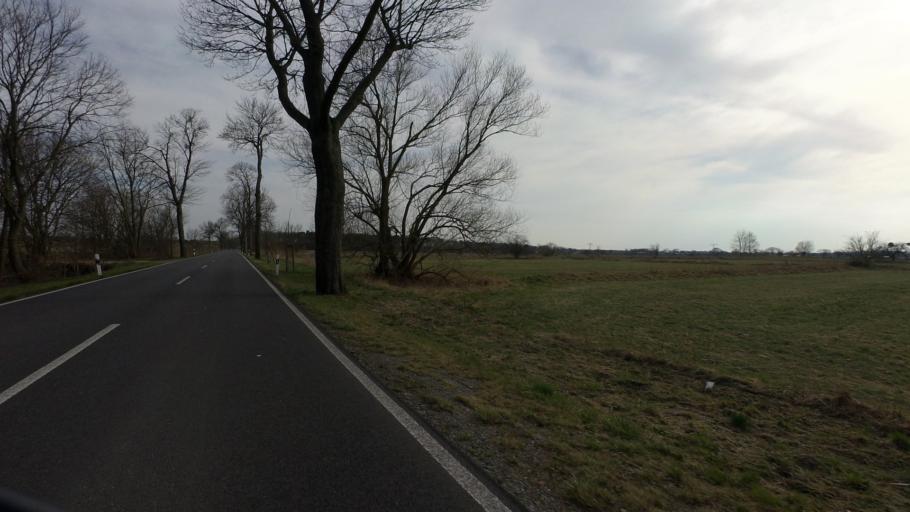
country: DE
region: Brandenburg
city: Stahnsdorf
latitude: 52.3493
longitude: 13.1951
